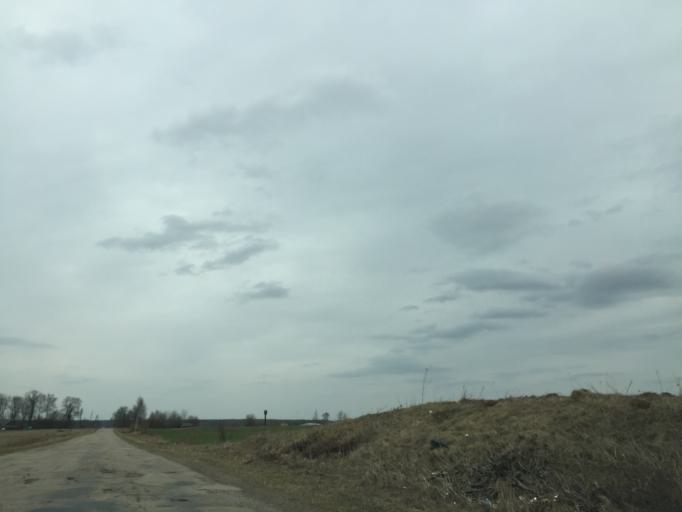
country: LV
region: Ilukste
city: Ilukste
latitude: 56.0160
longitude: 26.2717
